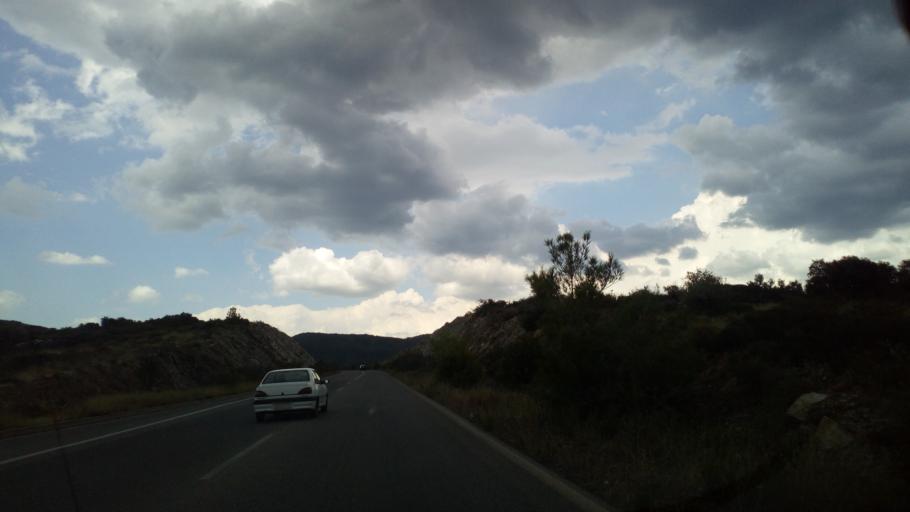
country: GR
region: Central Macedonia
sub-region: Nomos Chalkidikis
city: Polygyros
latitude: 40.3400
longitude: 23.4531
